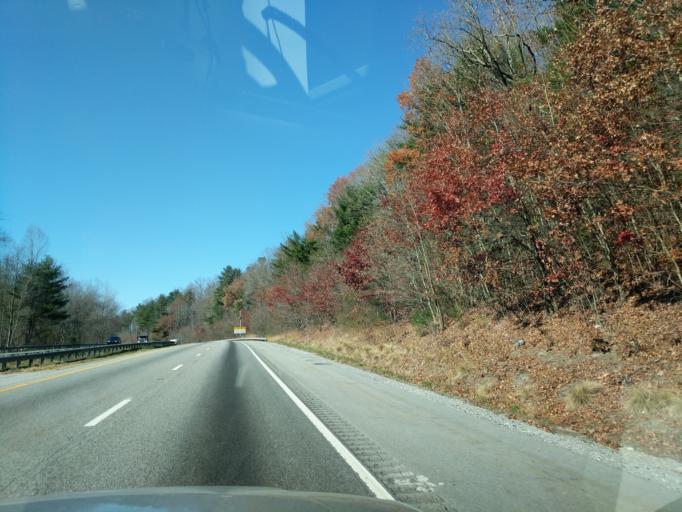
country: US
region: North Carolina
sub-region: Henderson County
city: East Flat Rock
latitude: 35.2755
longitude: -82.3859
